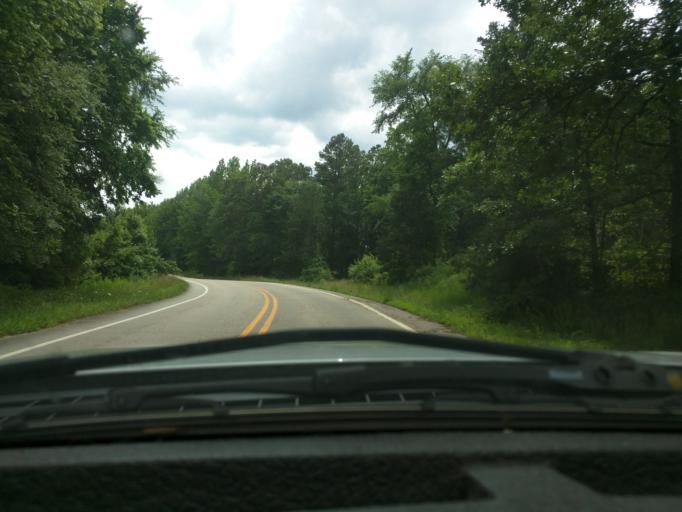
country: US
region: Arkansas
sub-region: Franklin County
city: Ozark
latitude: 35.6828
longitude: -93.8259
